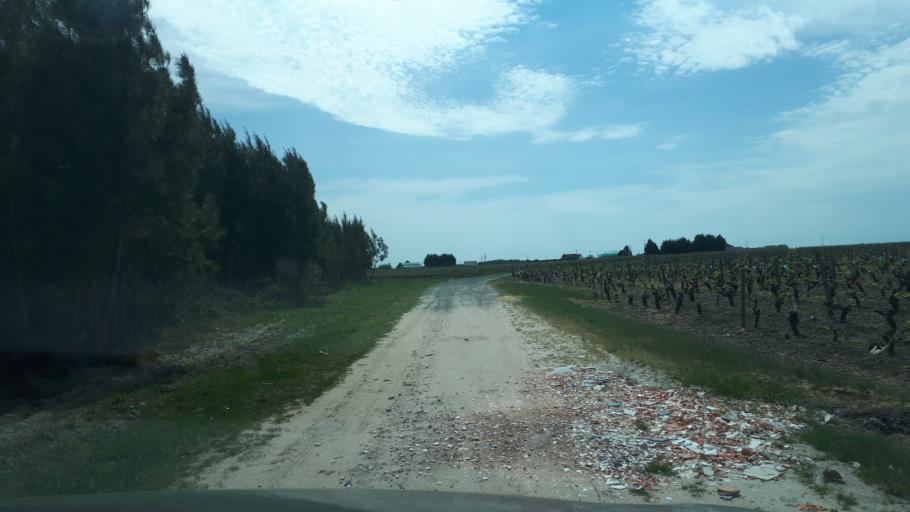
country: FR
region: Centre
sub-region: Departement du Loir-et-Cher
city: Saint-Romain-sur-Cher
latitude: 47.3580
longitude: 1.4297
